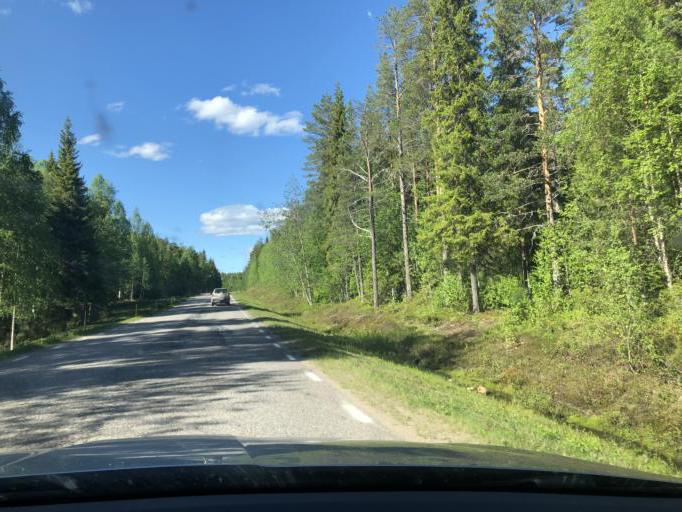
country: SE
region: Norrbotten
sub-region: Kalix Kommun
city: Kalix
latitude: 66.0050
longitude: 23.1432
